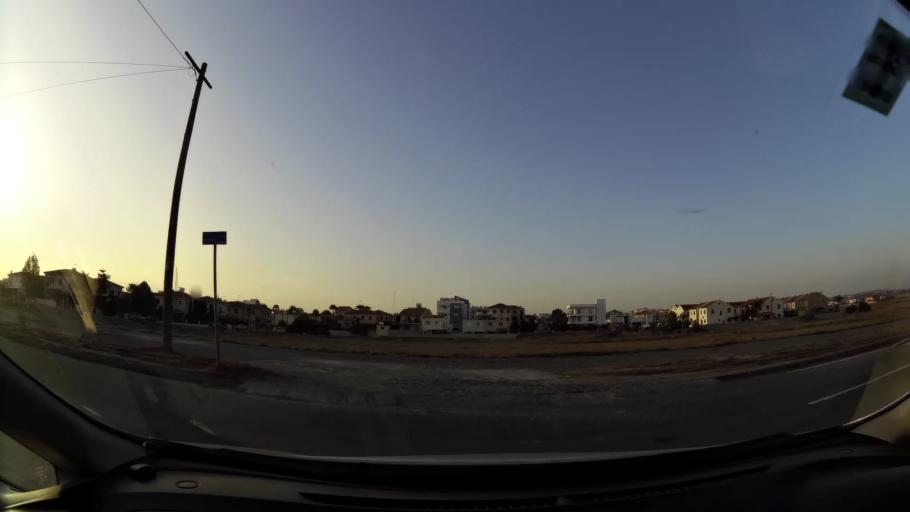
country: CY
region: Larnaka
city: Aradippou
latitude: 34.9209
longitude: 33.5896
